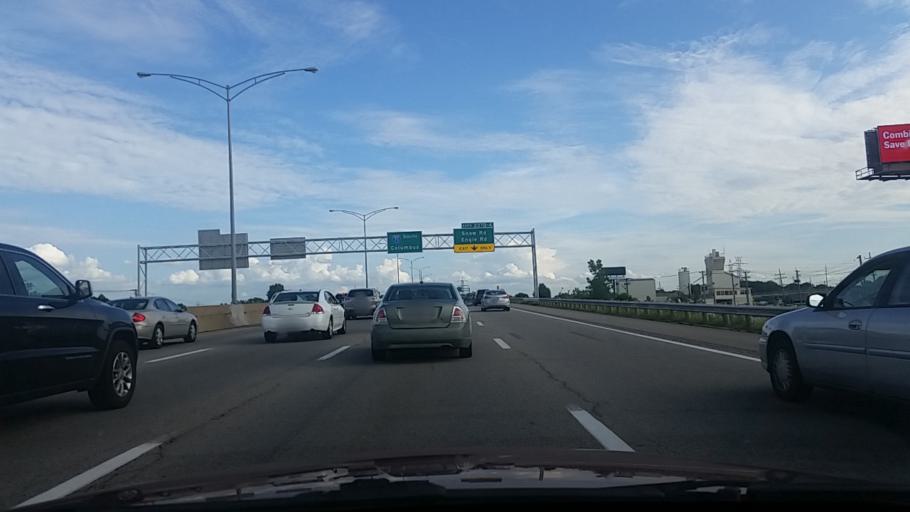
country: US
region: Ohio
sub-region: Cuyahoga County
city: Brook Park
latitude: 41.4096
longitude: -81.8182
